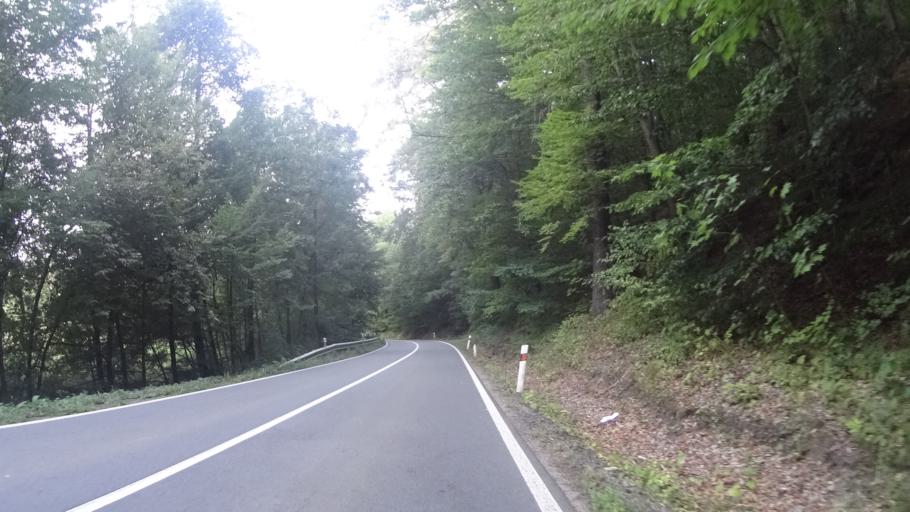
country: CZ
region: Olomoucky
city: Stity
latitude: 49.8654
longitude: 16.7370
